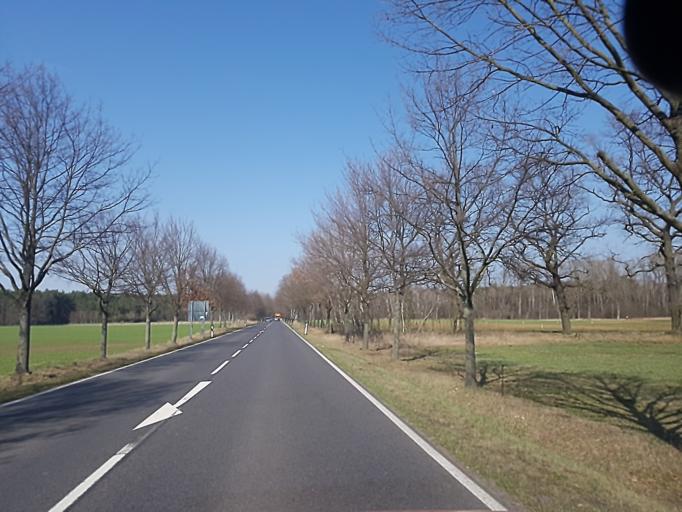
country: DE
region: Brandenburg
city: Tschernitz
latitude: 51.6552
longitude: 14.5889
